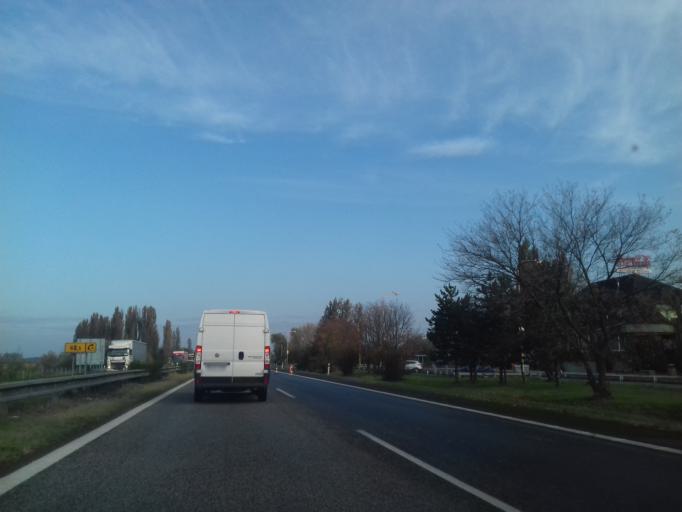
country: SK
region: Bratislavsky
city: Stupava
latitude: 48.2592
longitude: 17.0102
